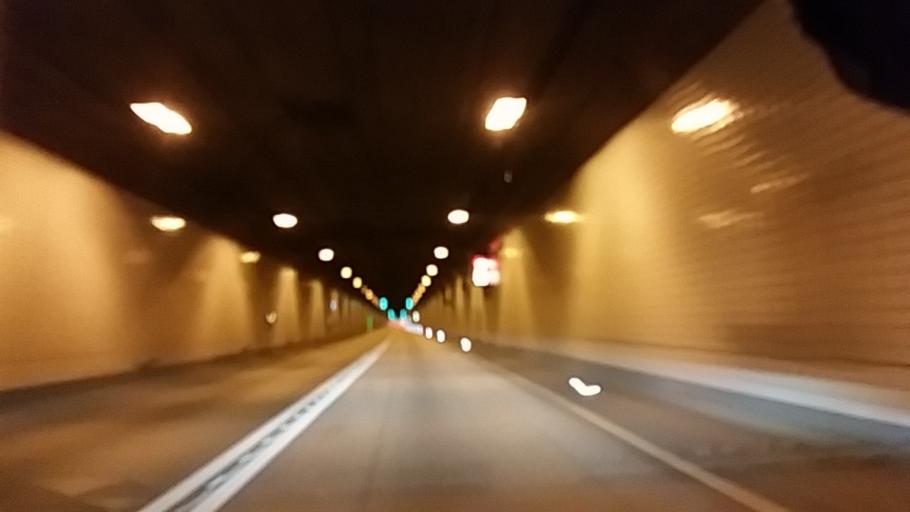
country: DE
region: Hamburg
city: Altona
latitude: 53.5482
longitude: 9.9025
